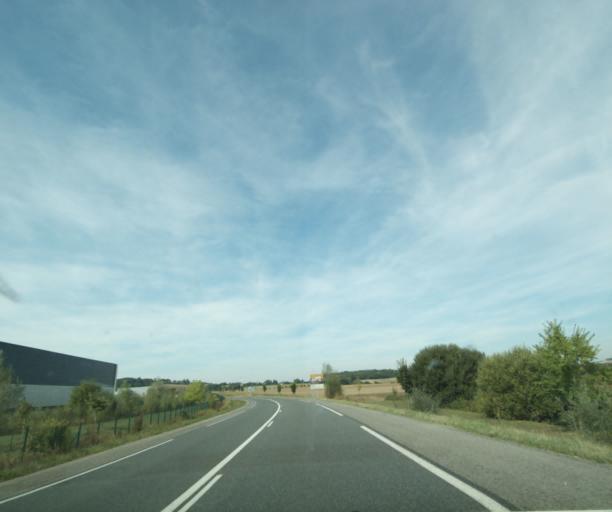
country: FR
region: Auvergne
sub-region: Departement de l'Allier
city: Saint-Germain-des-Fosses
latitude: 46.1831
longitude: 3.4603
